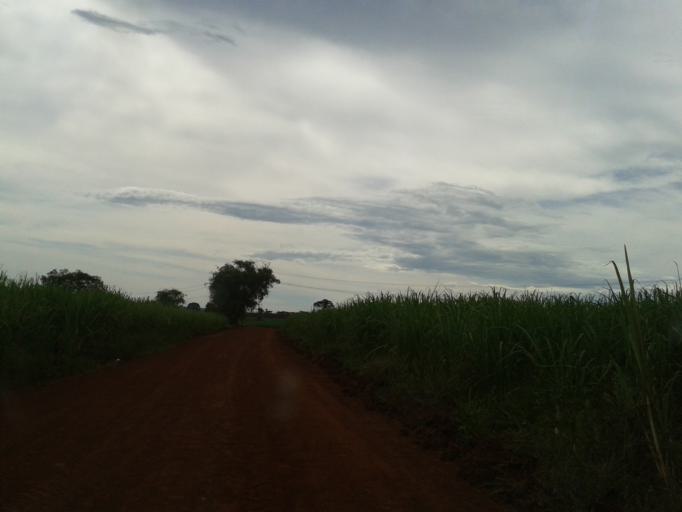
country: BR
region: Minas Gerais
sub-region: Centralina
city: Centralina
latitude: -18.6469
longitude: -49.3308
